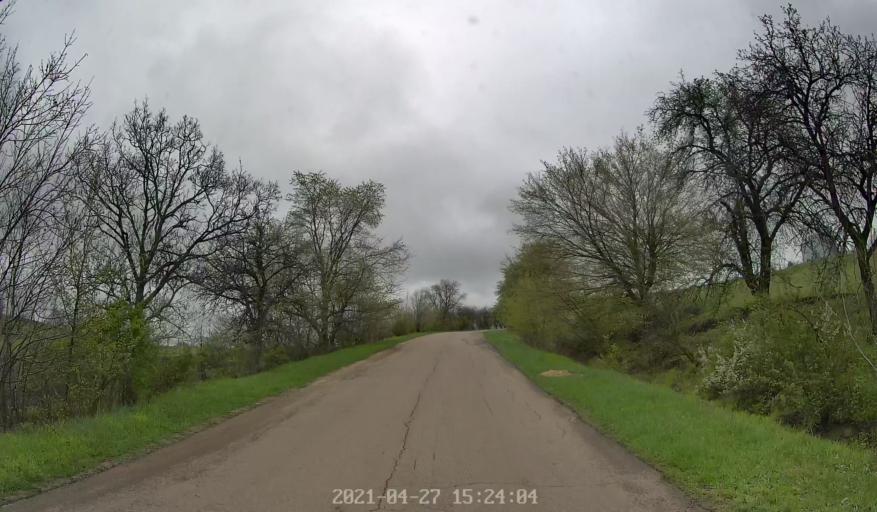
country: MD
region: Chisinau
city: Vadul lui Voda
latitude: 47.0164
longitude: 29.0246
